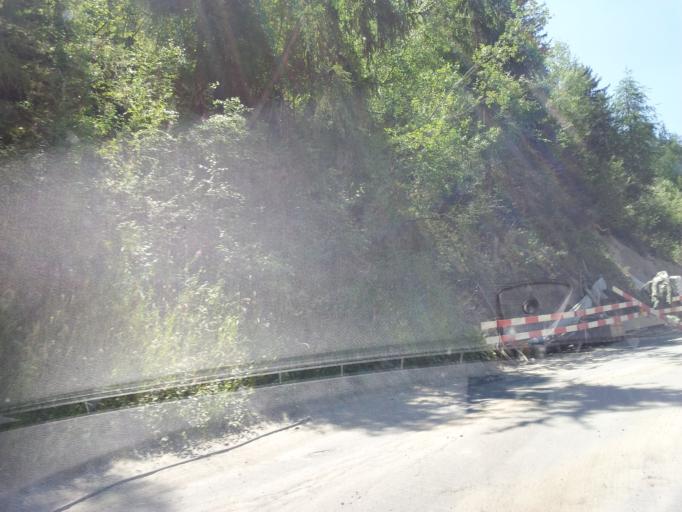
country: CH
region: Valais
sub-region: Visp District
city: Sankt Niklaus
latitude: 46.1838
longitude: 7.8200
